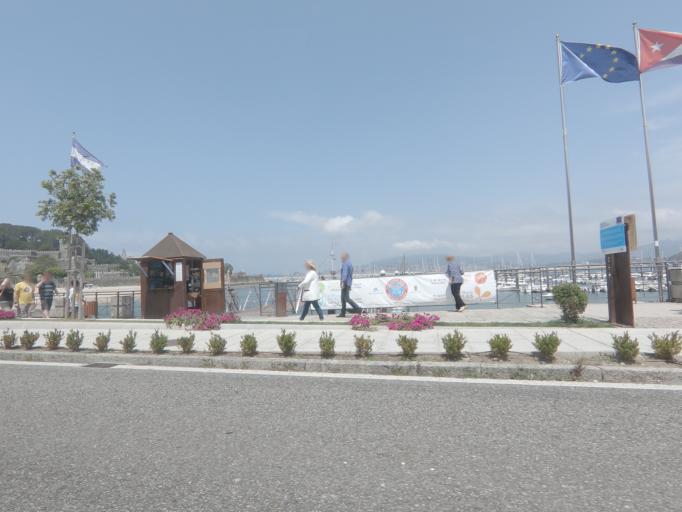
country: ES
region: Galicia
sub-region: Provincia de Pontevedra
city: Baiona
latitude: 42.1202
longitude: -8.8490
